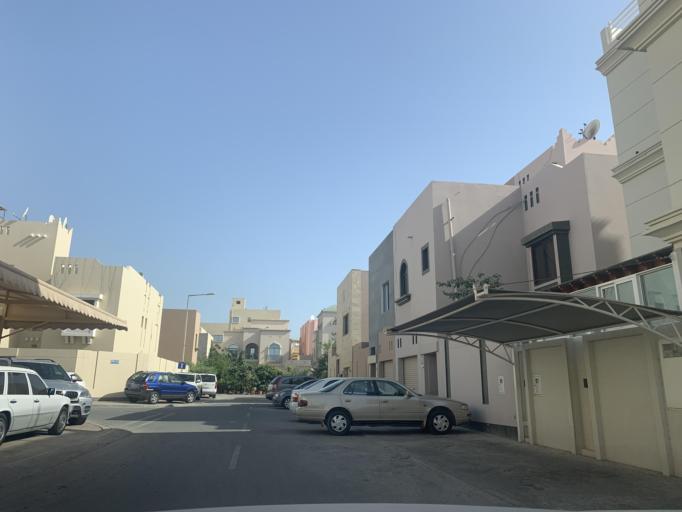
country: BH
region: Manama
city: Jidd Hafs
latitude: 26.2104
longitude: 50.5633
